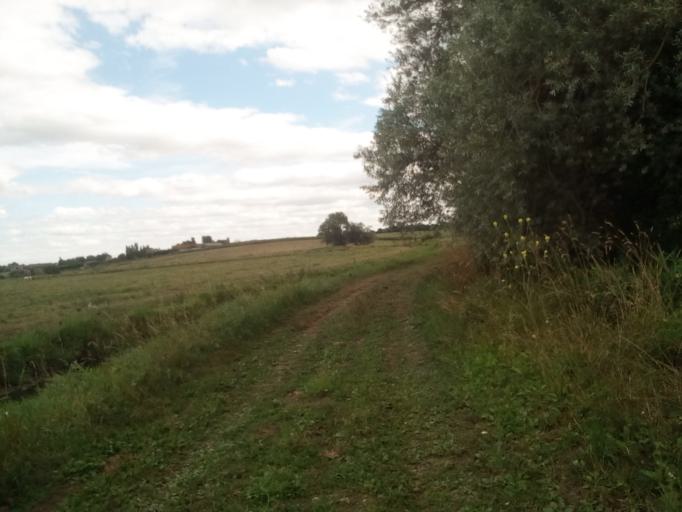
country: FR
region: Lower Normandy
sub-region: Departement du Calvados
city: Troarn
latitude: 49.1727
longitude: -0.1526
